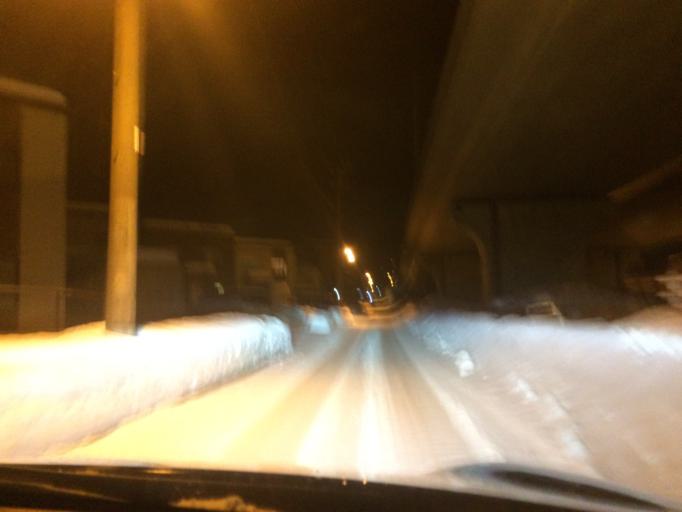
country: JP
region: Hokkaido
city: Ebetsu
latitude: 43.0484
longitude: 141.4704
